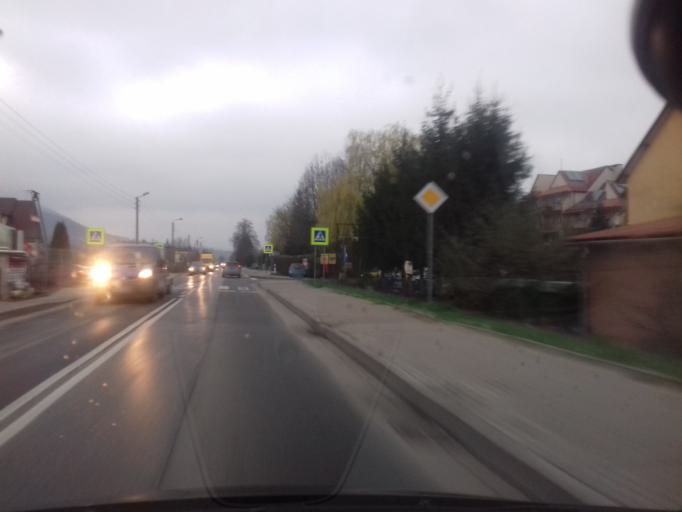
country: PL
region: Lesser Poland Voivodeship
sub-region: Powiat limanowski
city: Mszana Dolna
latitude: 49.6777
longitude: 20.0616
